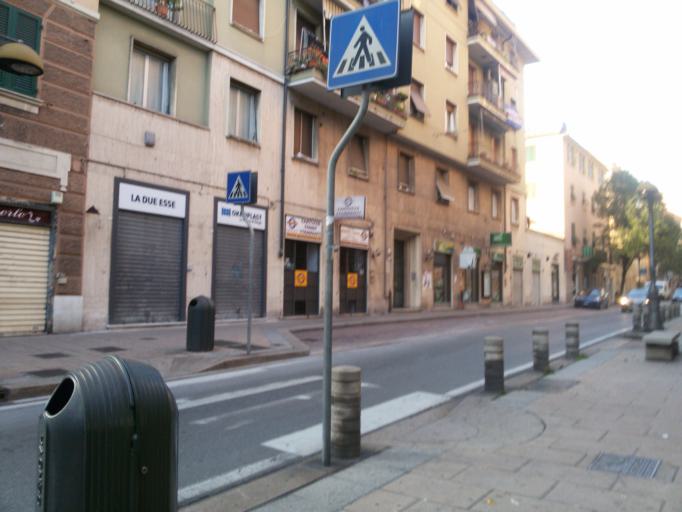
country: IT
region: Liguria
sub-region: Provincia di Genova
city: Genoa
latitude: 44.4312
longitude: 8.8920
